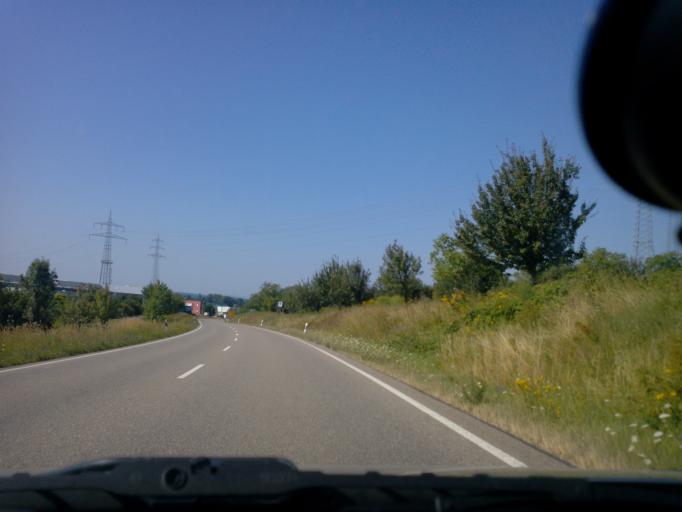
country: DE
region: Baden-Wuerttemberg
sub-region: Karlsruhe Region
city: Knittlingen
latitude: 49.0534
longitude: 8.7383
